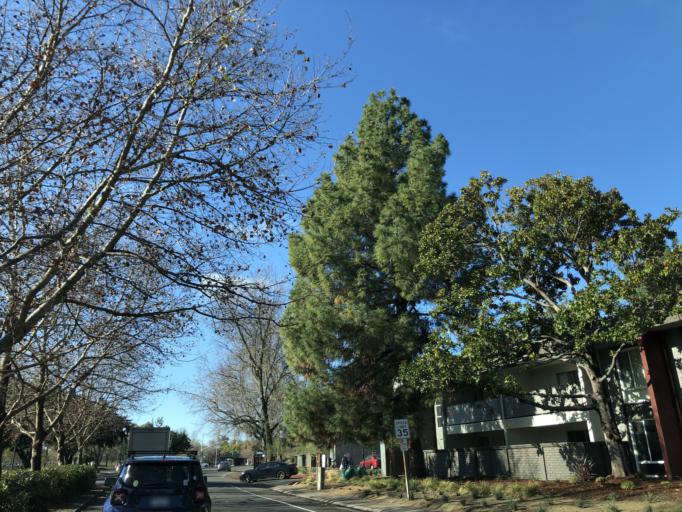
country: US
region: California
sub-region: Sacramento County
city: Rosemont
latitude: 38.5641
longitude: -121.3790
